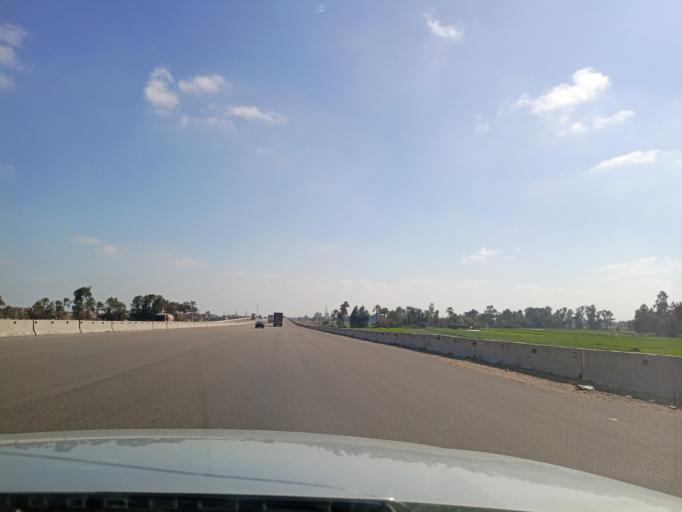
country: EG
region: Eastern Province
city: Mashtul as Suq
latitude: 30.4637
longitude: 31.3185
